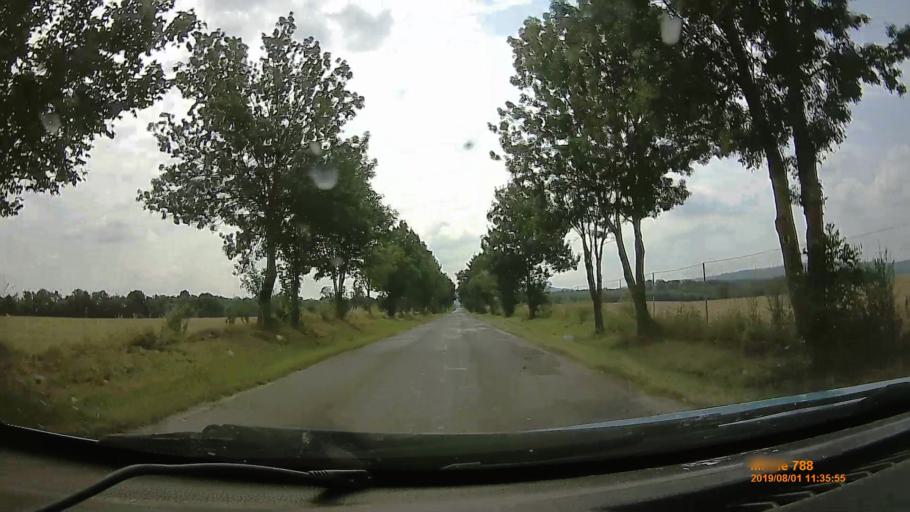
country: HU
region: Baranya
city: Villany
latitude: 45.9226
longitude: 18.3714
